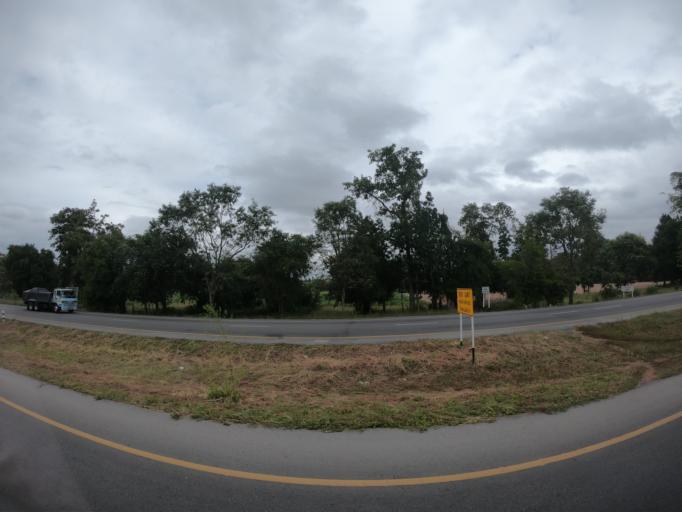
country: TH
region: Khon Kaen
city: Ban Phai
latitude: 16.0444
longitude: 102.8559
